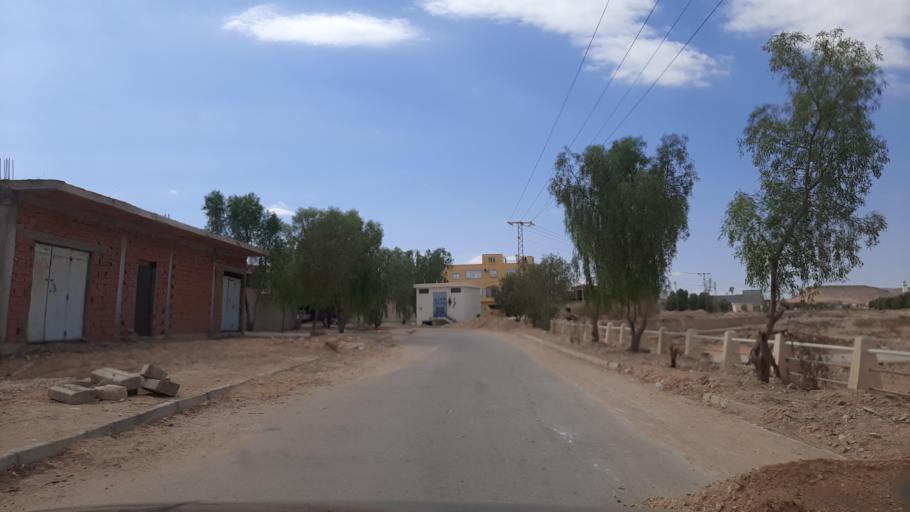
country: TN
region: Tataouine
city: Tataouine
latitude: 32.9351
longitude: 10.4495
